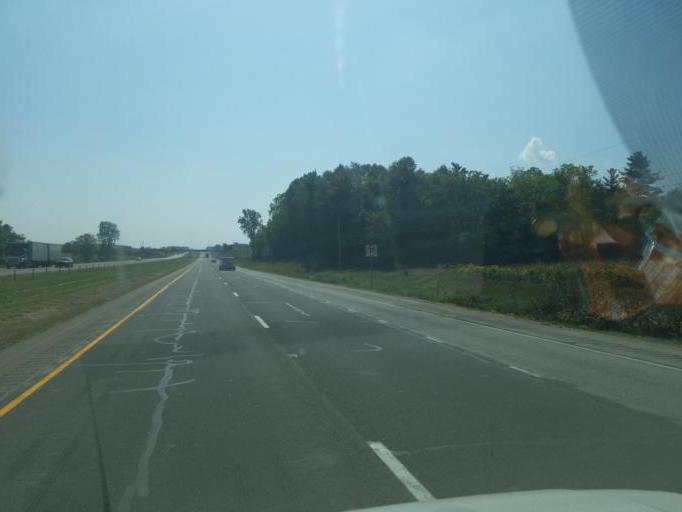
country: US
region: Indiana
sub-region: Steuben County
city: Angola
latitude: 41.5753
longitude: -85.0585
